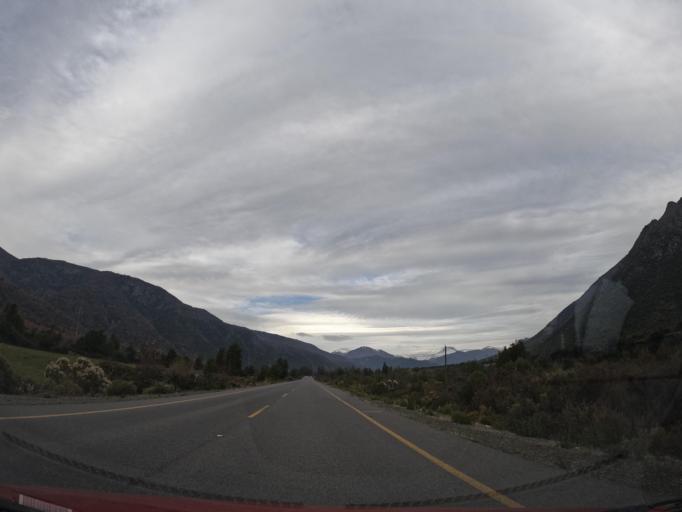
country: CL
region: Maule
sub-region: Provincia de Linares
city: Colbun
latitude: -35.7212
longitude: -71.0302
